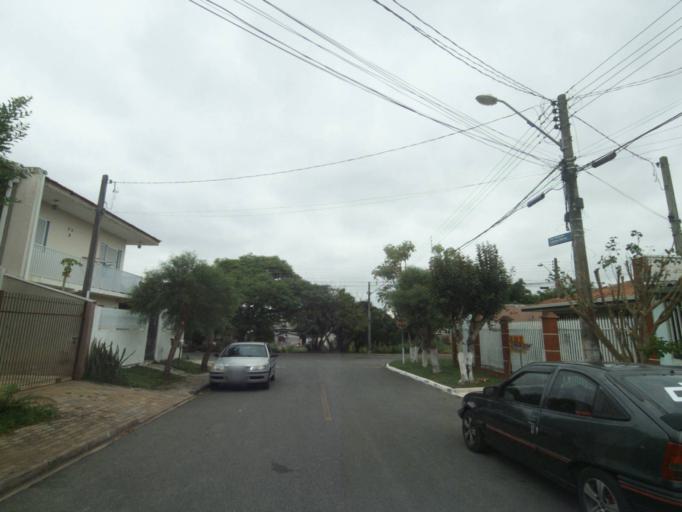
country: BR
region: Parana
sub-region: Sao Jose Dos Pinhais
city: Sao Jose dos Pinhais
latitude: -25.5384
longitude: -49.2655
